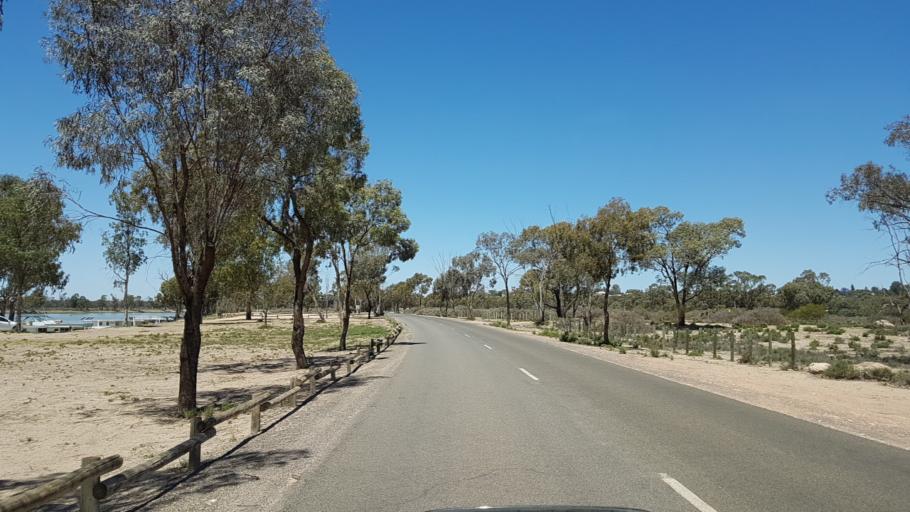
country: AU
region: South Australia
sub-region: Loxton Waikerie
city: Waikerie
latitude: -34.1696
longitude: 139.9761
